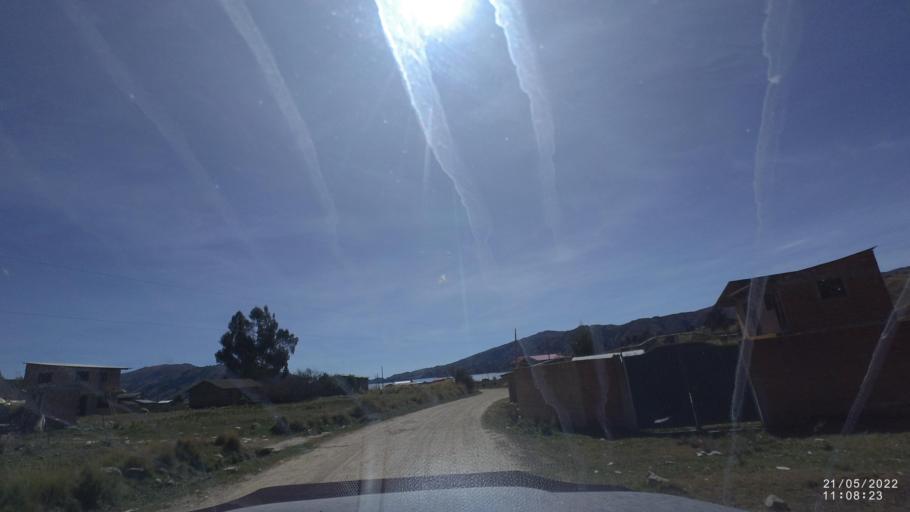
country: BO
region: Cochabamba
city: Colomi
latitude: -17.3070
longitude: -65.9118
